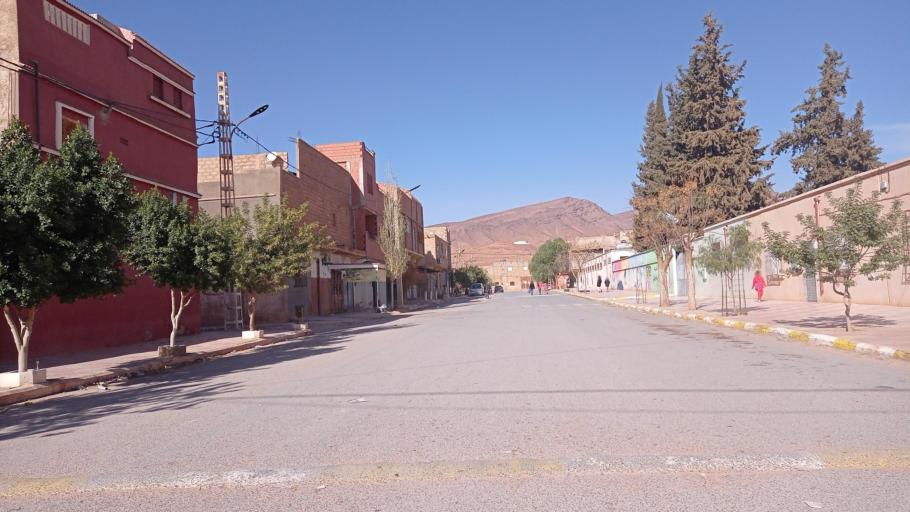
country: DZ
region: Wilaya de Naama
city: Ain Sefra
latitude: 32.7625
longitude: -0.5805
